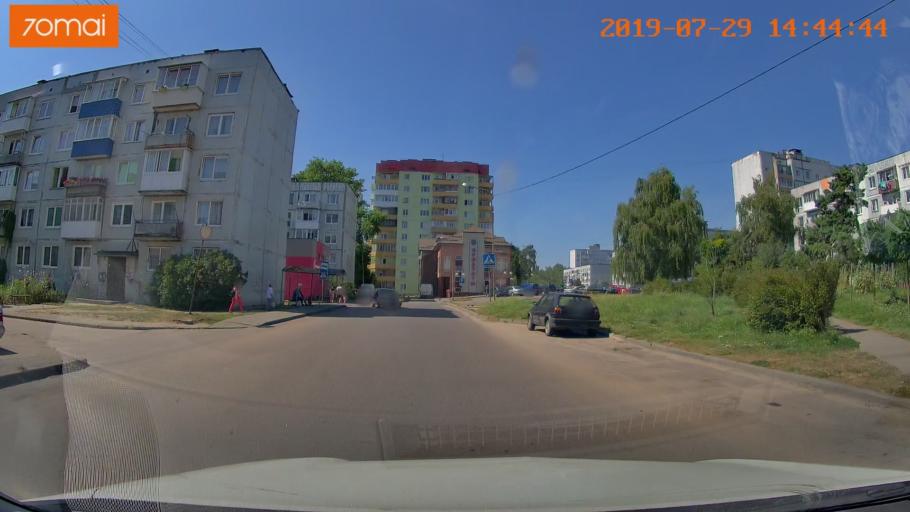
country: RU
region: Kaliningrad
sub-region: Gorod Kaliningrad
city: Baltiysk
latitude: 54.6630
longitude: 19.9074
